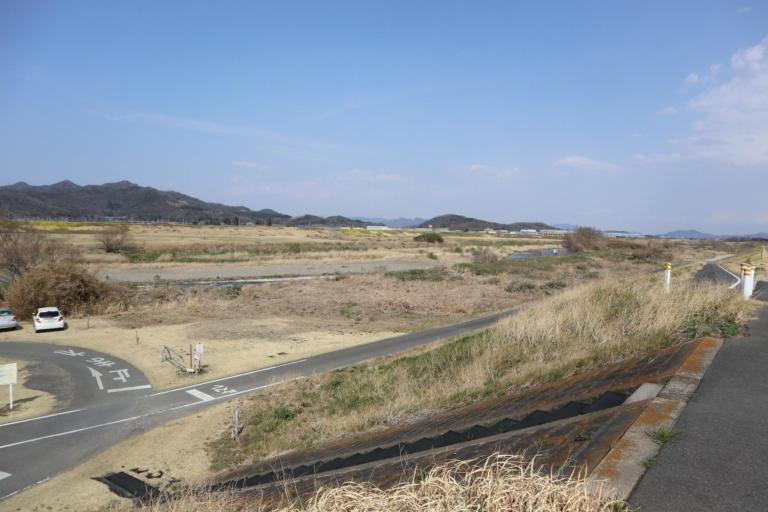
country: JP
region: Tochigi
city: Ashikaga
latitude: 36.3010
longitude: 139.4993
